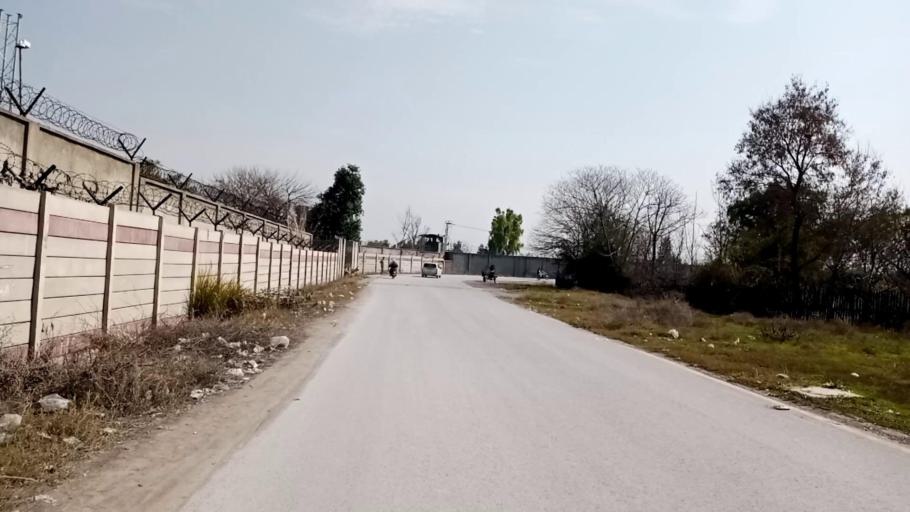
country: PK
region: Khyber Pakhtunkhwa
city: Peshawar
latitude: 33.9942
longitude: 71.5098
